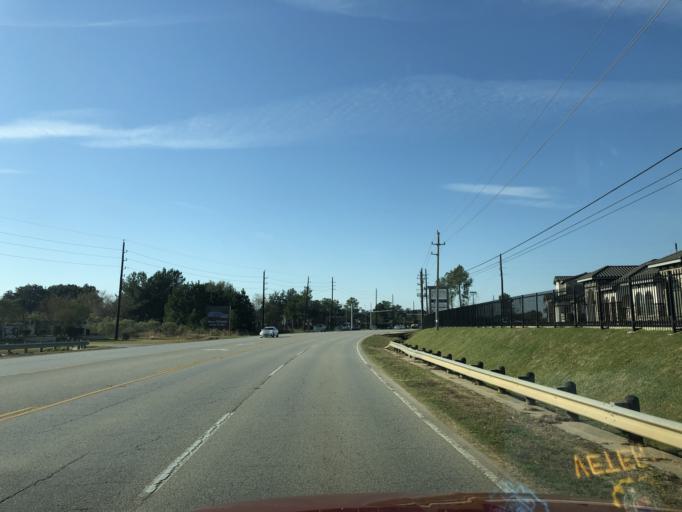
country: US
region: Texas
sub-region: Harris County
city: Tomball
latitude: 30.0398
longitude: -95.5468
